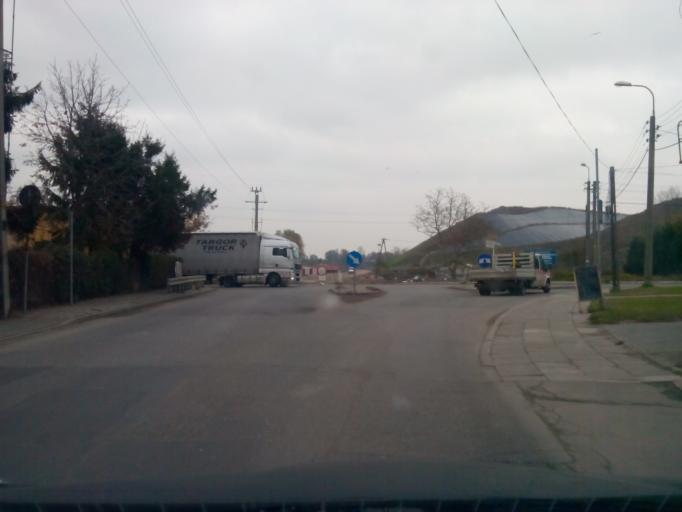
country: PL
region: Masovian Voivodeship
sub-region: Powiat pruszkowski
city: Pruszkow
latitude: 52.1745
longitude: 20.7712
